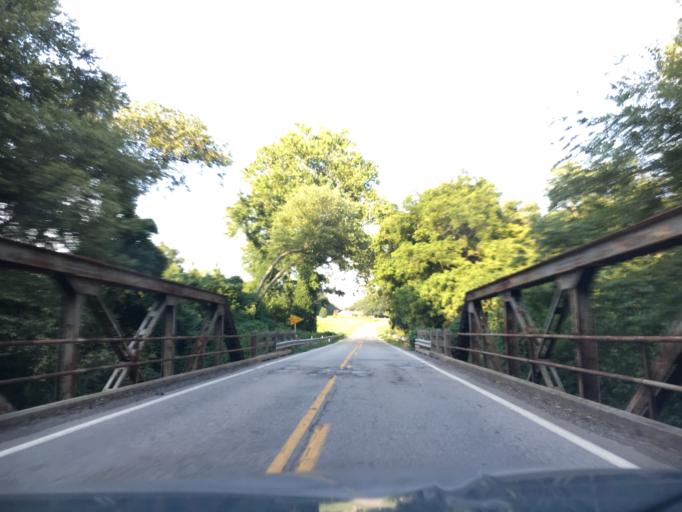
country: US
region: Virginia
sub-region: Pittsylvania County
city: Chatham
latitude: 36.8269
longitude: -79.3199
